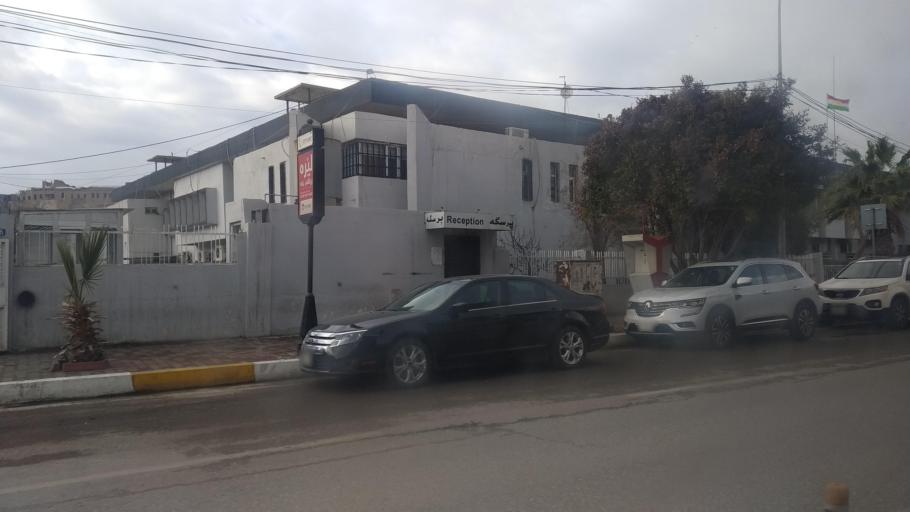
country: IQ
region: Arbil
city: Erbil
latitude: 36.1942
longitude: 44.0125
